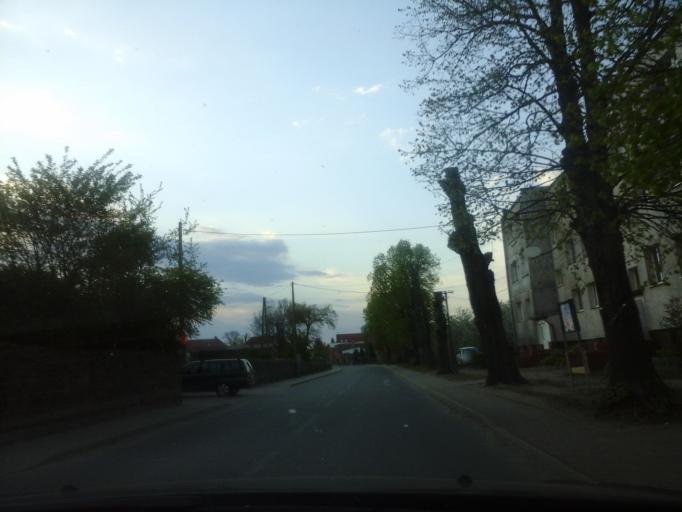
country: PL
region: West Pomeranian Voivodeship
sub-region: Powiat choszczenski
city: Pelczyce
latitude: 53.0225
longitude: 15.3676
